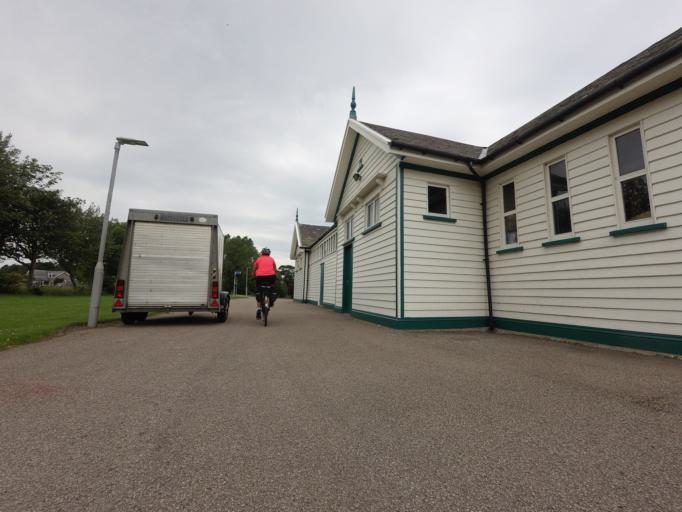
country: GB
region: Scotland
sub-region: Aberdeenshire
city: Portsoy
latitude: 57.6791
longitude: -2.6903
